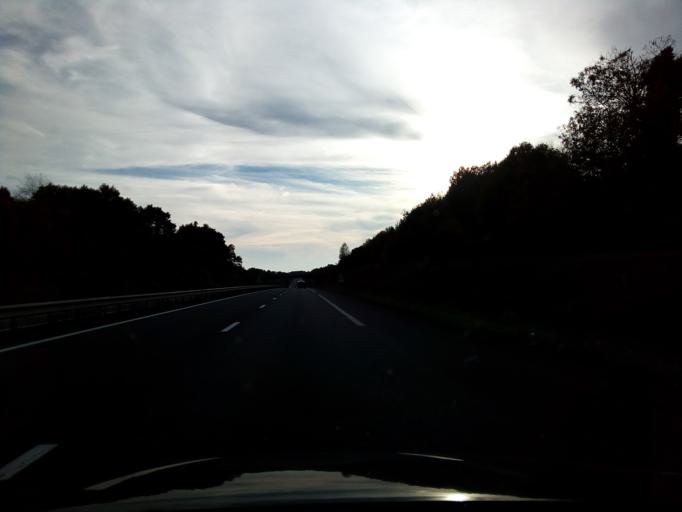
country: FR
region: Poitou-Charentes
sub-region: Departement de la Charente
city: Chasseneuil-sur-Bonnieure
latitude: 45.8087
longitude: 0.4463
